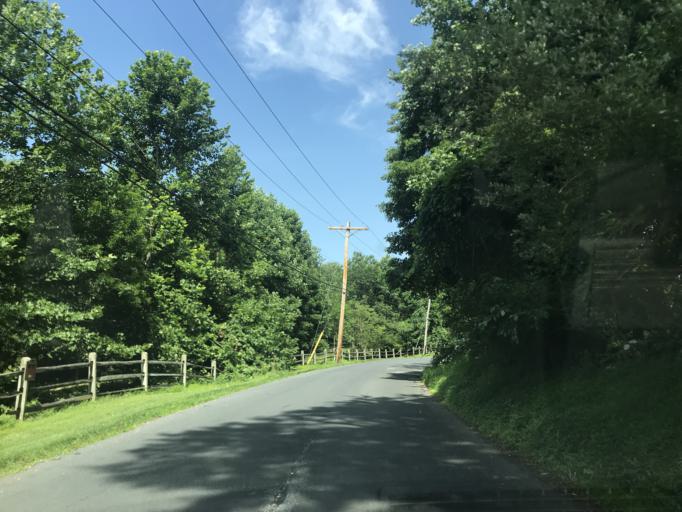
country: US
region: Delaware
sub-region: New Castle County
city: Greenville
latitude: 39.8056
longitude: -75.6398
